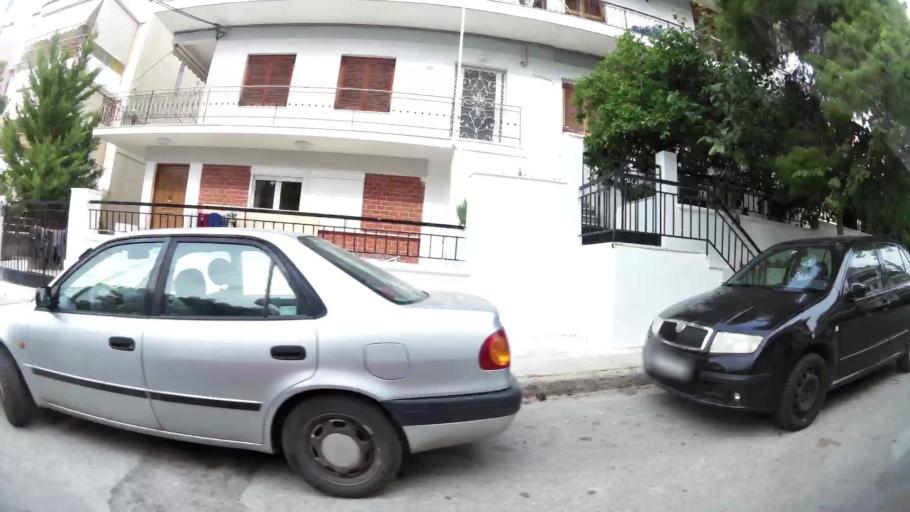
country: GR
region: Attica
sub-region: Nomarchia Athinas
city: Chaidari
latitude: 38.0169
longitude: 23.6444
